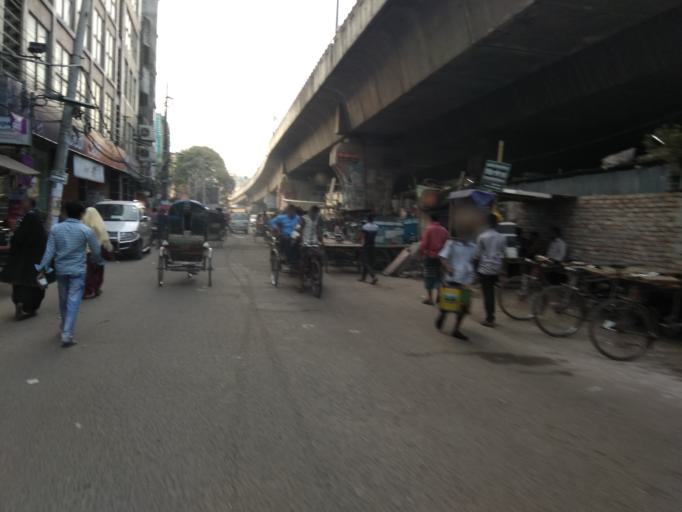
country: BD
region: Dhaka
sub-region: Dhaka
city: Dhaka
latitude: 23.7218
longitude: 90.4162
